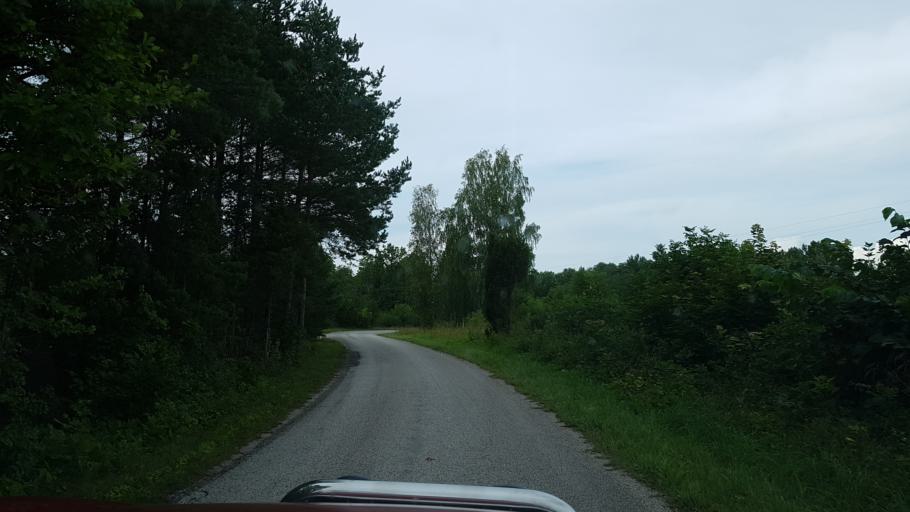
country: EE
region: Laeaene
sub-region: Ridala Parish
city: Uuemoisa
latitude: 58.9854
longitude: 23.6677
